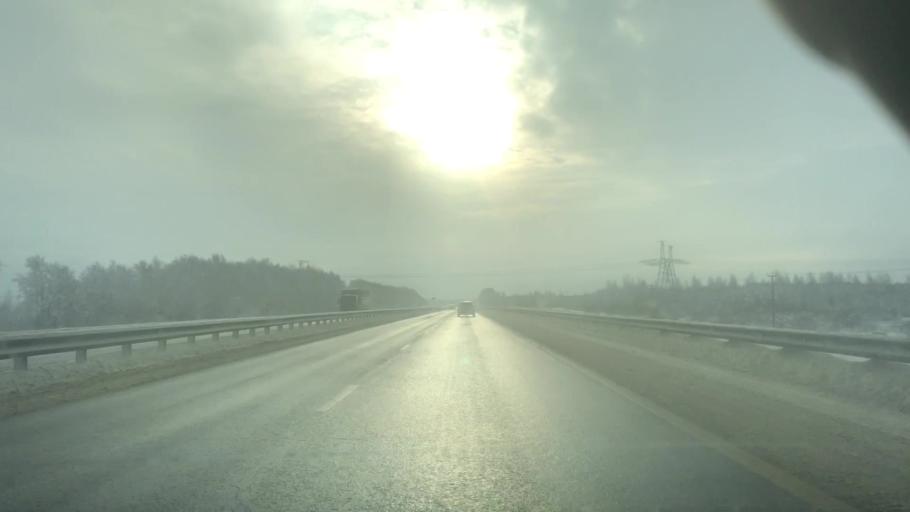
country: RU
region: Tula
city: Venev
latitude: 54.2937
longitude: 38.1577
